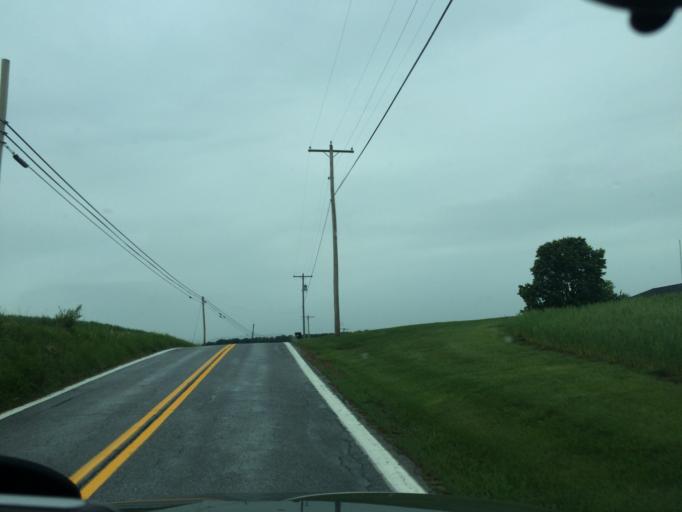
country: US
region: Maryland
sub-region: Carroll County
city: Taneytown
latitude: 39.6050
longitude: -77.2477
